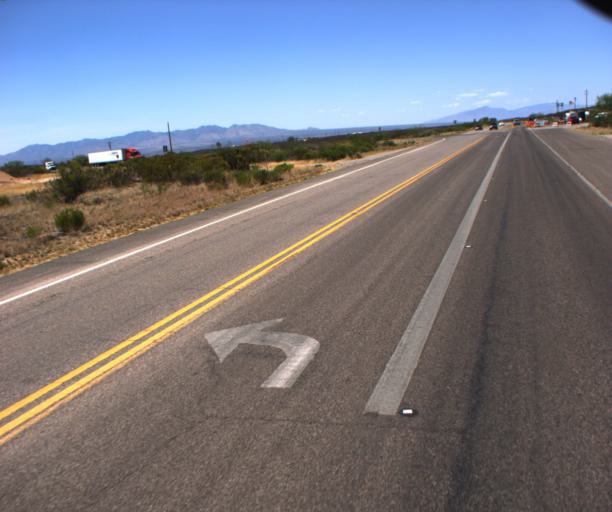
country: US
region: Arizona
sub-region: Cochise County
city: Tombstone
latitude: 31.7479
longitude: -110.0964
